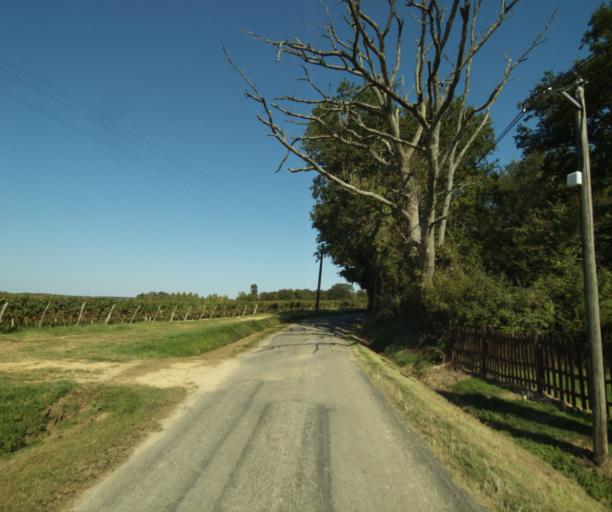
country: FR
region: Midi-Pyrenees
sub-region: Departement du Gers
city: Cazaubon
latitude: 43.9229
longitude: -0.0267
